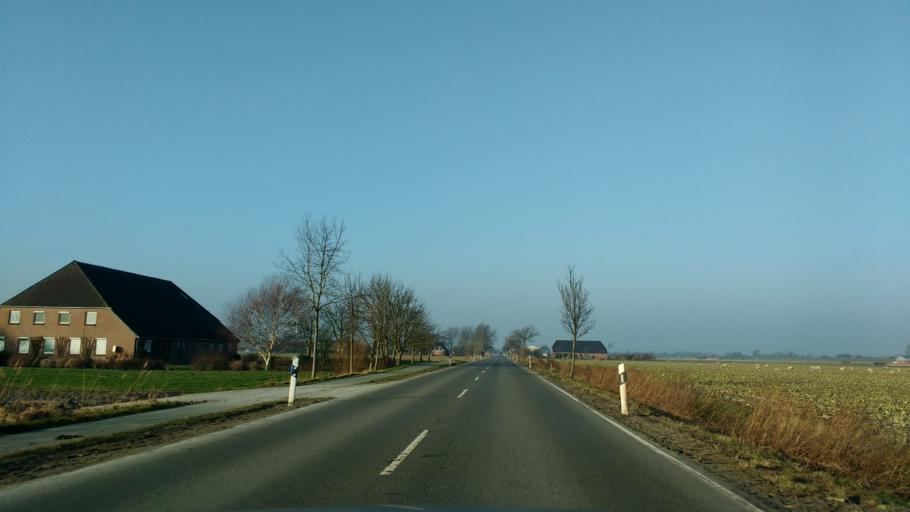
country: DE
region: Schleswig-Holstein
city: Friedrichskoog
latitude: 53.9912
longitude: 8.9035
